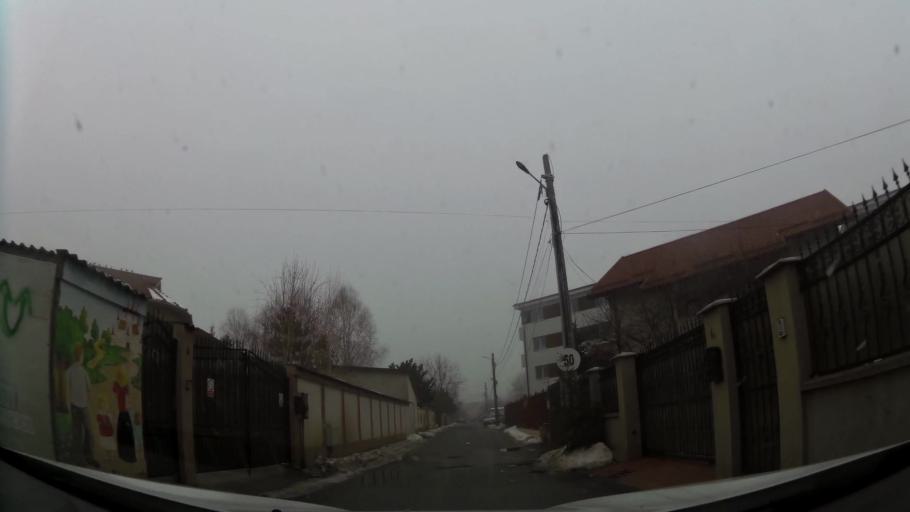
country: RO
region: Ilfov
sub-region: Comuna Chiajna
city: Rosu
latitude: 44.4548
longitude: 25.9951
